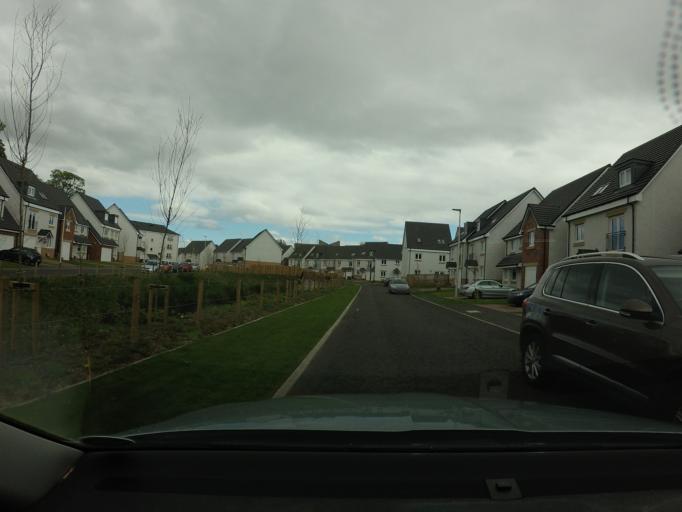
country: GB
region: Scotland
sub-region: Edinburgh
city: Kirkliston
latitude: 55.9534
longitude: -3.4093
